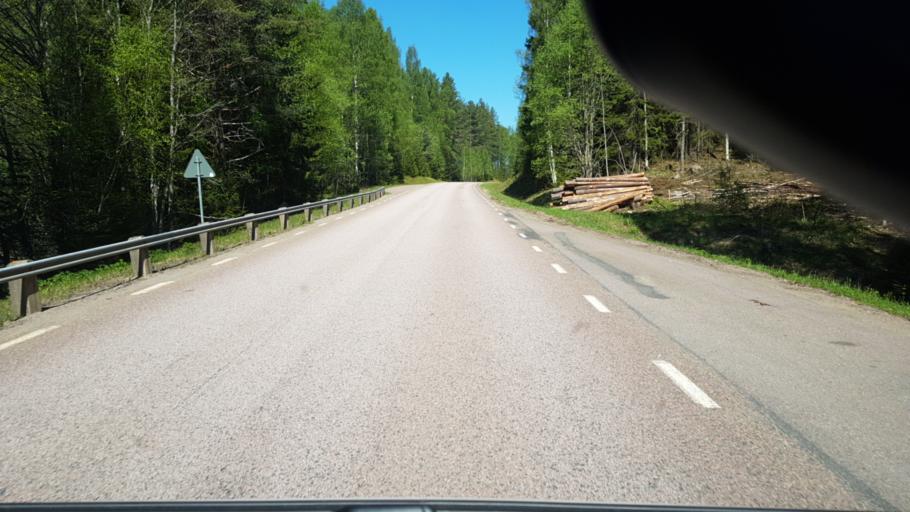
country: SE
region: Vaermland
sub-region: Arvika Kommun
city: Arvika
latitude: 59.9197
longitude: 12.6552
